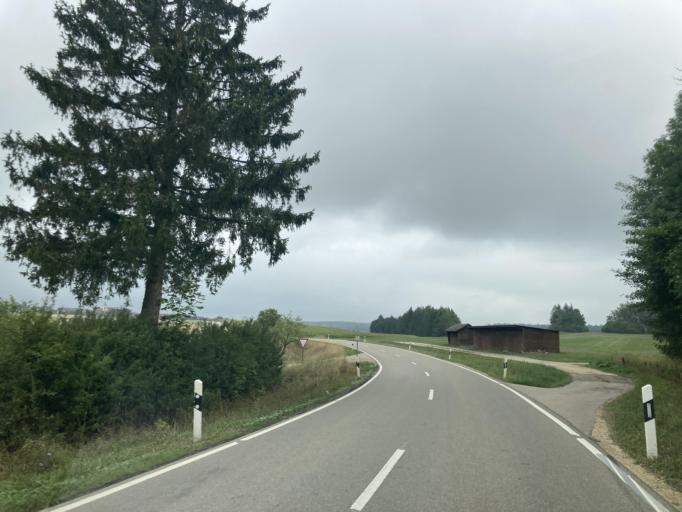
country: DE
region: Bavaria
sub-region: Swabia
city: Forheim
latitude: 48.7749
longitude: 10.4122
